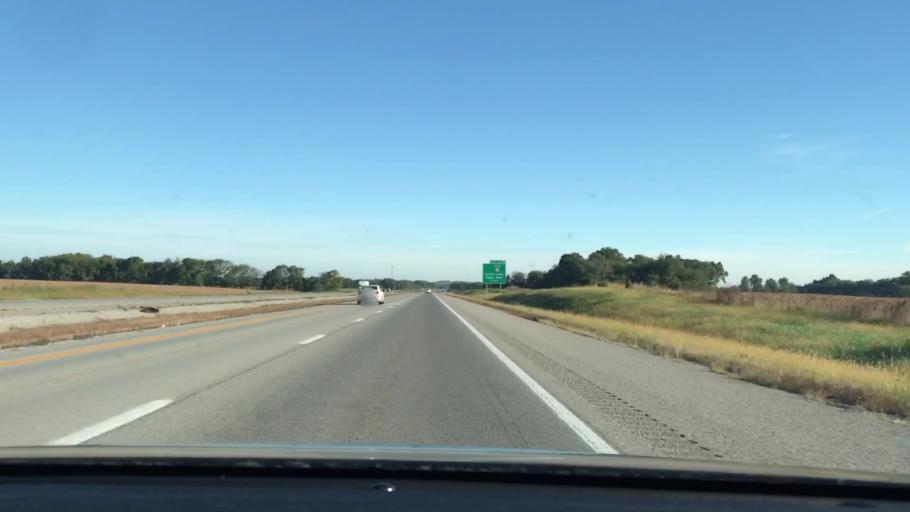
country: US
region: Kentucky
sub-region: Christian County
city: Hopkinsville
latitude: 36.7890
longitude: -87.4955
